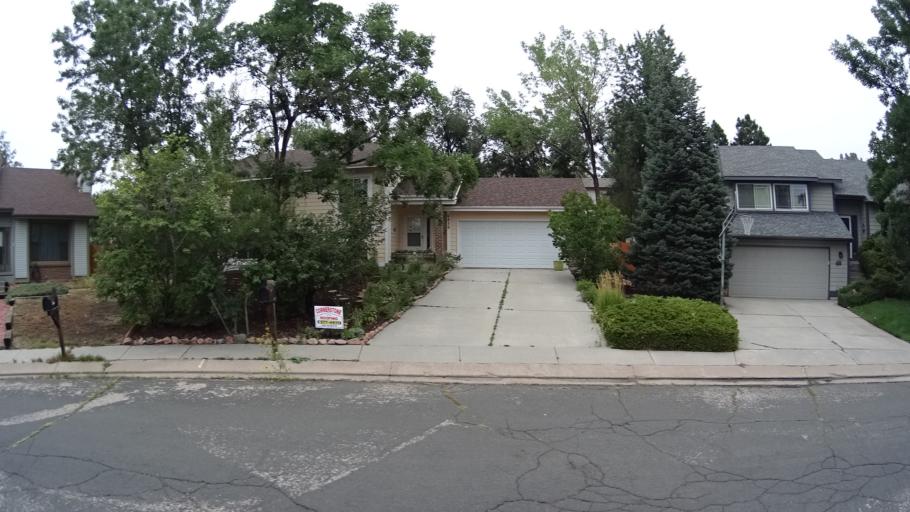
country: US
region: Colorado
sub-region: El Paso County
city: Cimarron Hills
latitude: 38.9318
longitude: -104.7715
